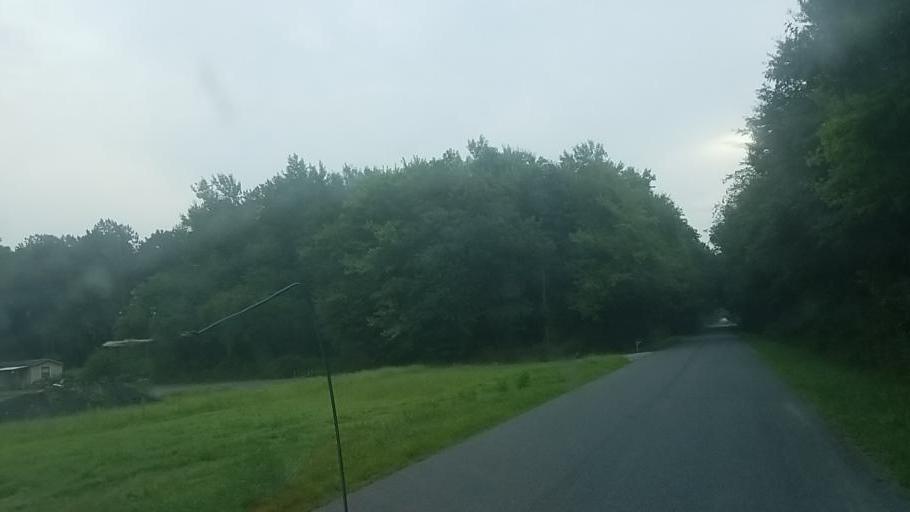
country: US
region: Maryland
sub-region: Wicomico County
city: Pittsville
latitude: 38.4521
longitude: -75.3883
